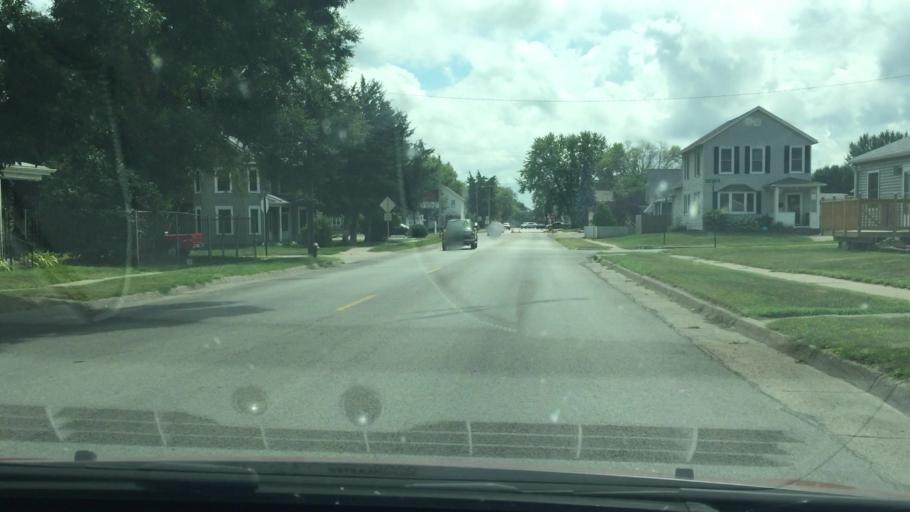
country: US
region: Iowa
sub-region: Muscatine County
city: Muscatine
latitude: 41.4333
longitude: -91.0429
